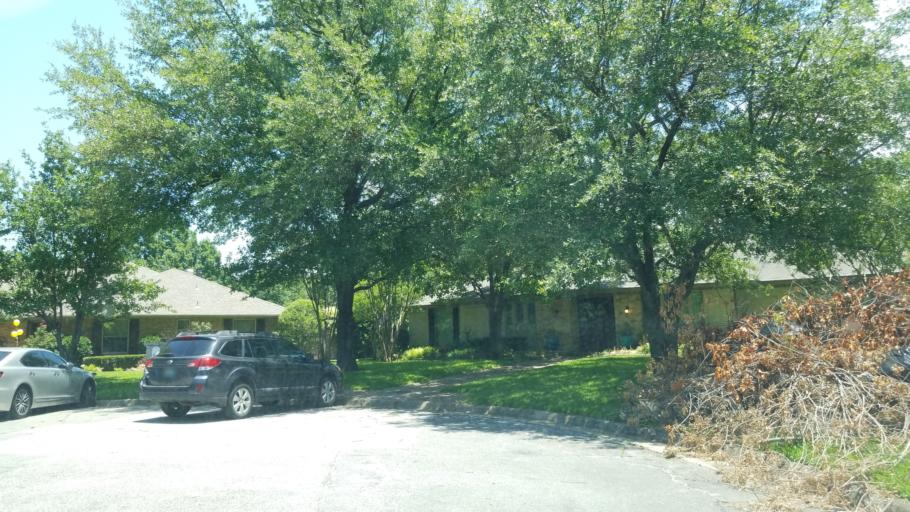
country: US
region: Texas
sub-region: Dallas County
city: University Park
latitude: 32.8910
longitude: -96.8369
